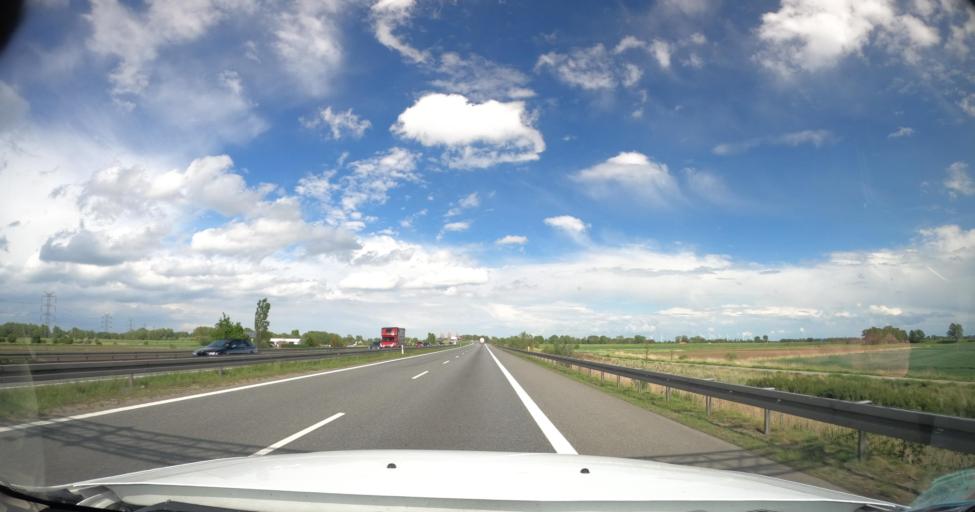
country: PL
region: Pomeranian Voivodeship
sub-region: Gdansk
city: Gdansk
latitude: 54.3112
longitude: 18.6719
